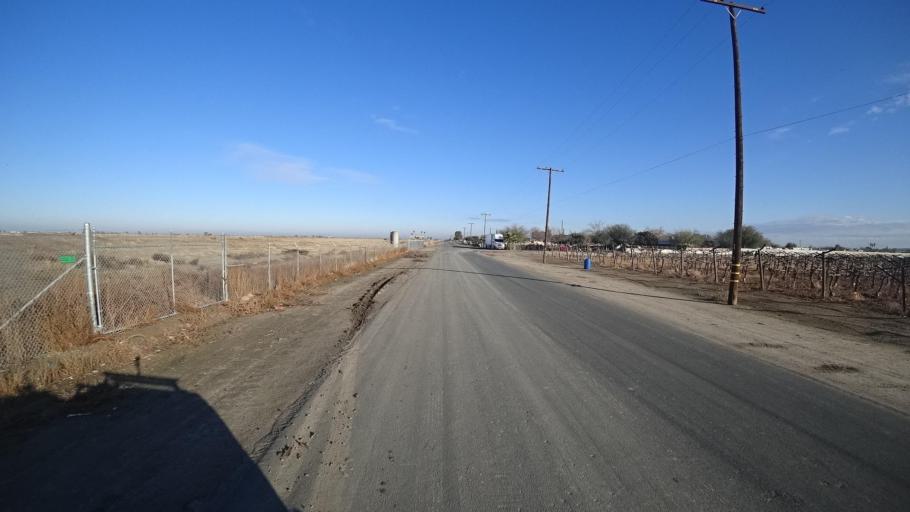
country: US
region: California
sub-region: Kern County
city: Delano
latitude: 35.7680
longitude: -119.2852
